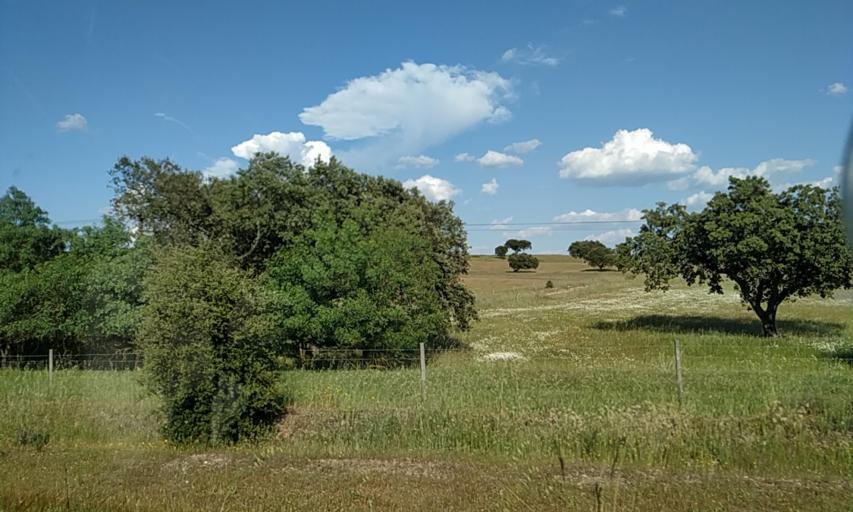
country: PT
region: Portalegre
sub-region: Fronteira
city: Fronteira
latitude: 39.0132
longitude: -7.4673
